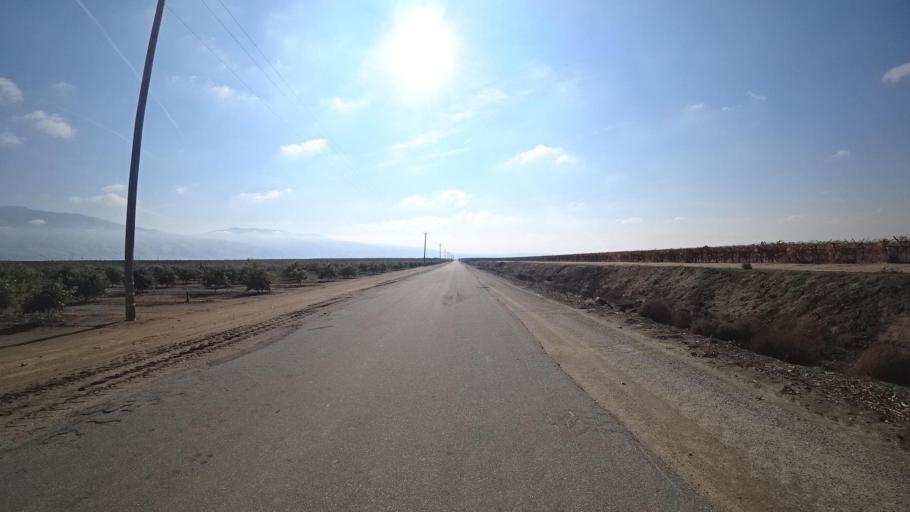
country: US
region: California
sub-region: Kern County
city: Arvin
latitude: 35.2785
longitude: -118.7889
